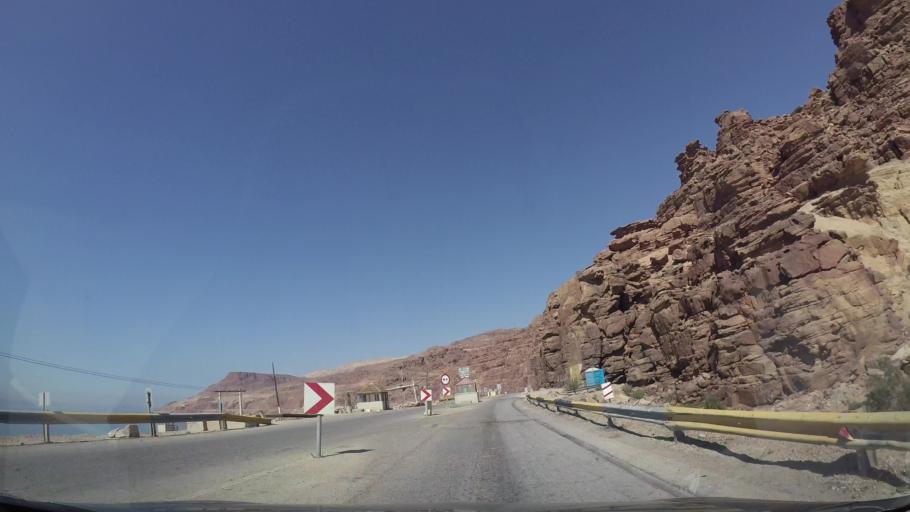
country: JO
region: Karak
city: Al Qasr
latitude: 31.4692
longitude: 35.5732
